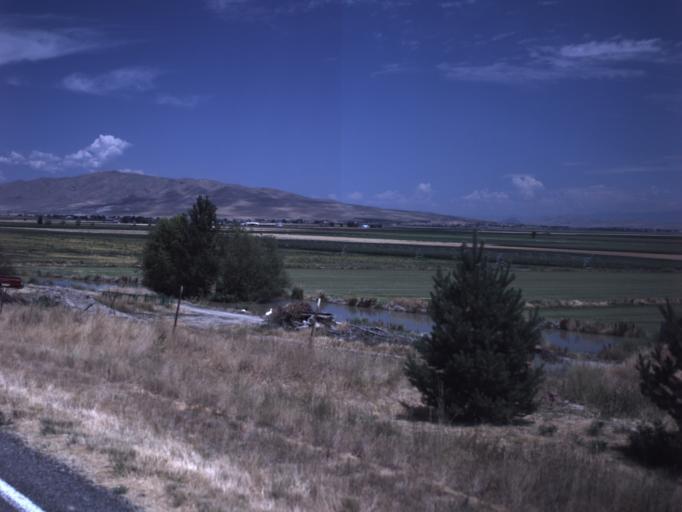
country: US
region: Utah
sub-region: Box Elder County
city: Tremonton
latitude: 41.6600
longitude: -112.2962
